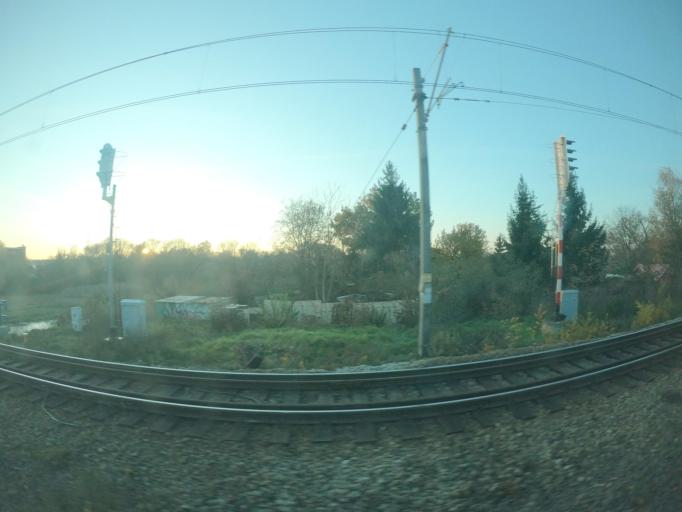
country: PL
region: Lubusz
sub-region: Powiat gorzowski
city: Kostrzyn nad Odra
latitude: 52.5828
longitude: 14.6428
